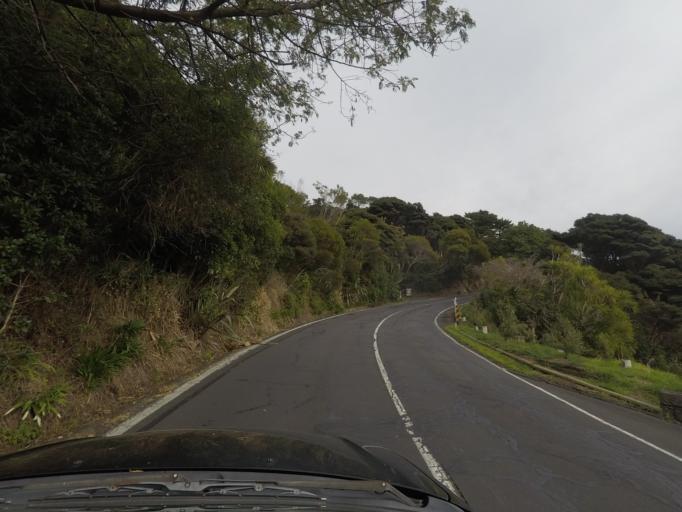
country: NZ
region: Auckland
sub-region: Auckland
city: Muriwai Beach
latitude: -36.9607
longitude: 174.4772
